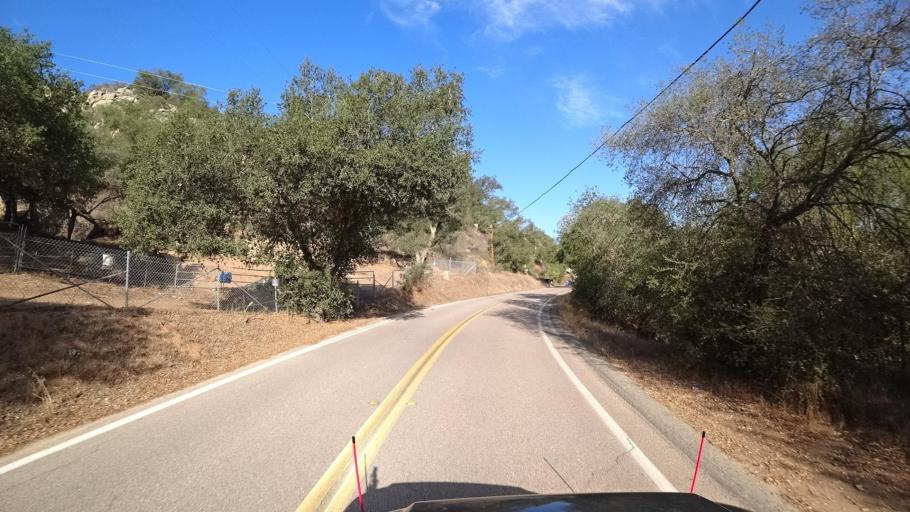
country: US
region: California
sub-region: San Diego County
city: Valley Center
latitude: 33.1663
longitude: -116.9977
